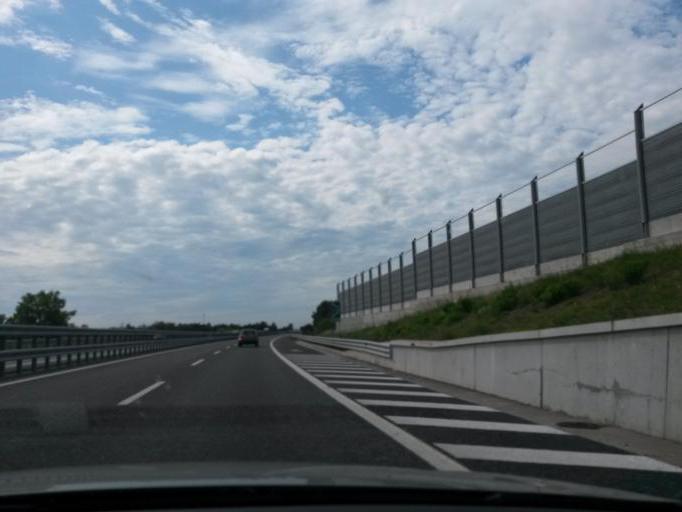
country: IT
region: Tuscany
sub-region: Provincia di Livorno
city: S.P. in Palazzi
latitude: 43.3567
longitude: 10.5128
